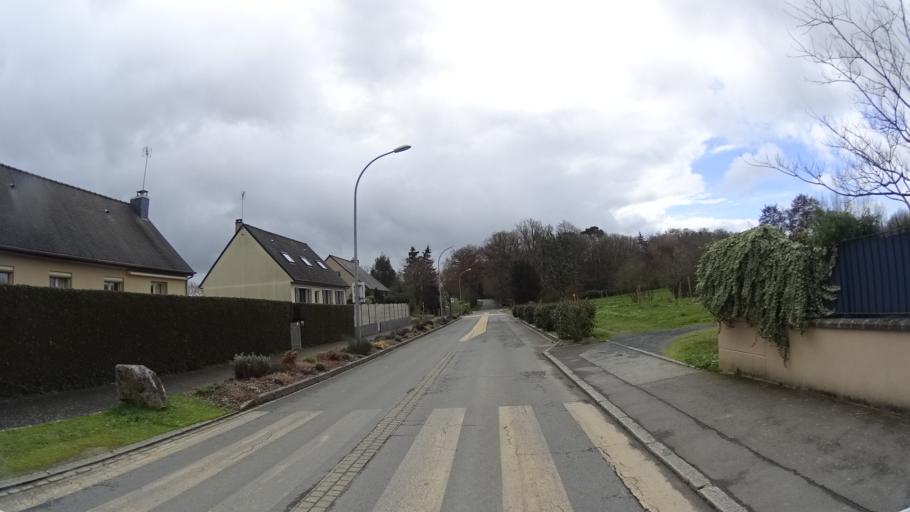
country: FR
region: Brittany
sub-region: Departement d'Ille-et-Vilaine
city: Saint-Gilles
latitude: 48.1516
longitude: -1.8300
